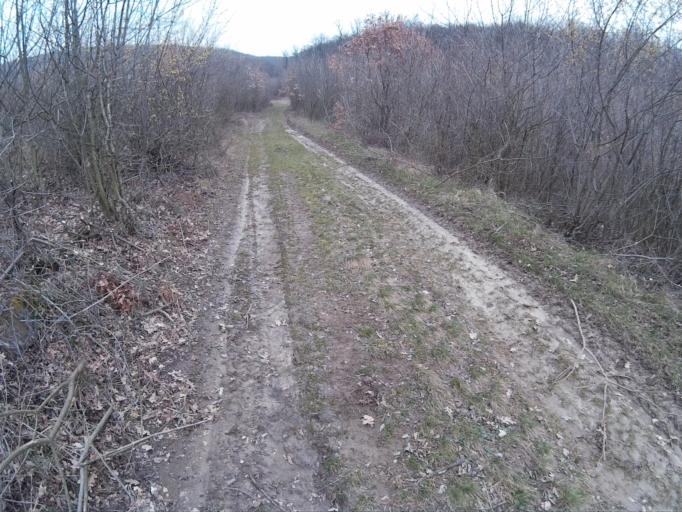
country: HU
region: Veszprem
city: Veszprem
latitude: 47.1705
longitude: 17.8696
